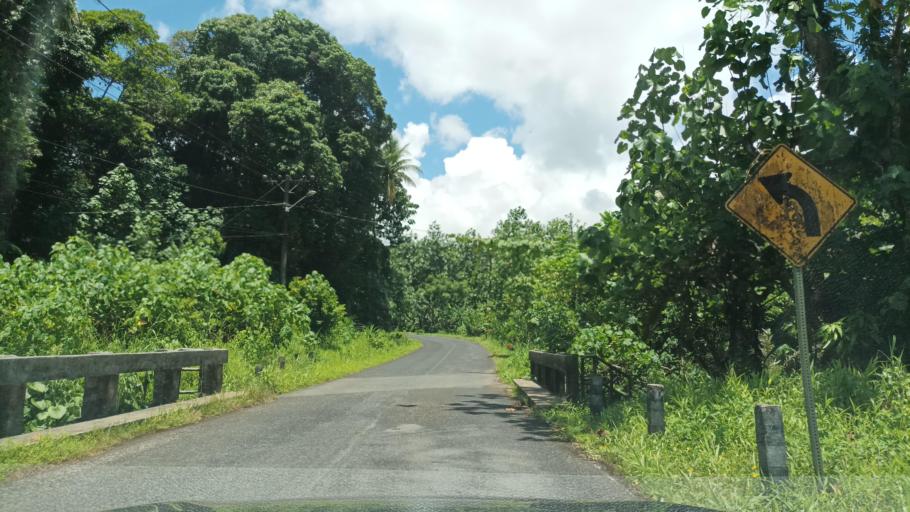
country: FM
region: Pohnpei
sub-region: Madolenihm Municipality
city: Madolenihm Municipality Government
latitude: 6.8738
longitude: 158.2866
